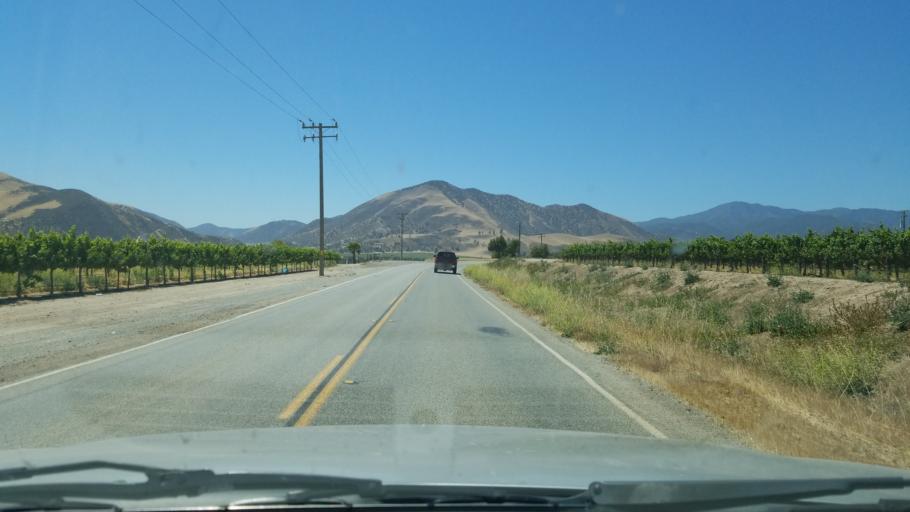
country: US
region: California
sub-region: Monterey County
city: Greenfield
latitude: 36.3057
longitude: -121.3117
